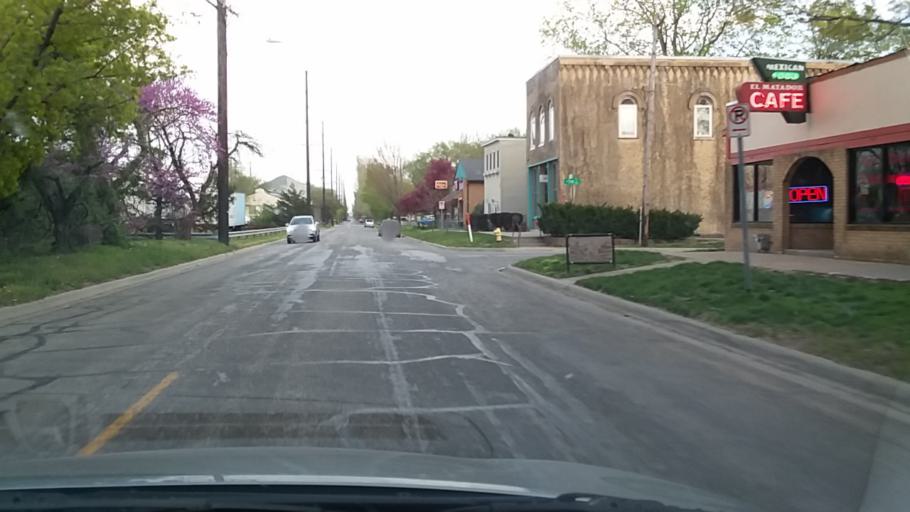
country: US
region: Kansas
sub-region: Douglas County
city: Lawrence
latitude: 38.9778
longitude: -95.2292
